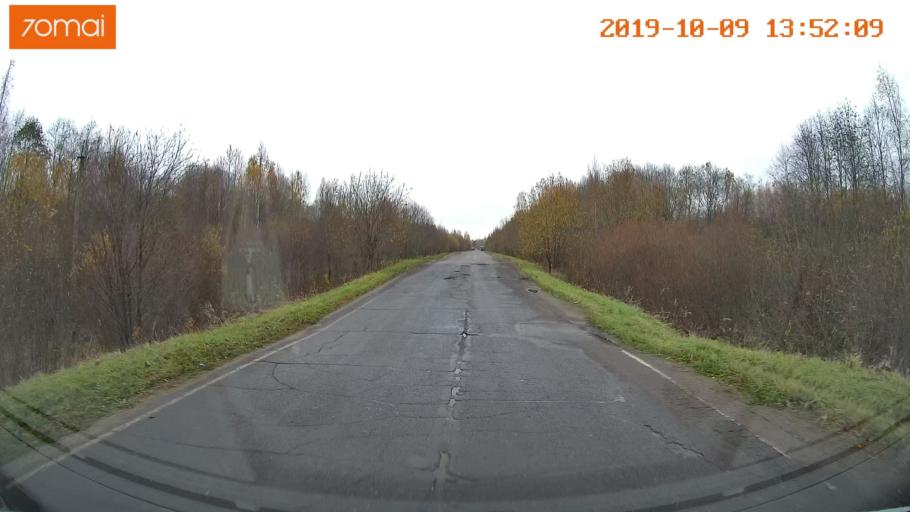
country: RU
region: Kostroma
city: Buy
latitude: 58.4108
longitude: 41.2465
